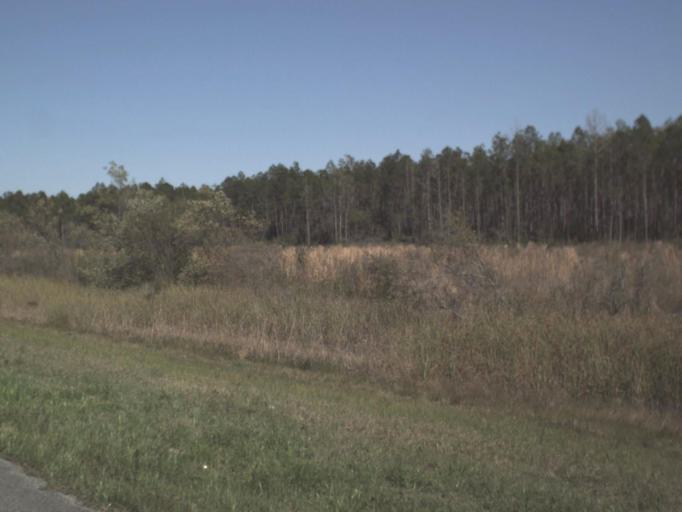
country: US
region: Florida
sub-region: Gulf County
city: Port Saint Joe
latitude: 29.9152
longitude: -85.2022
